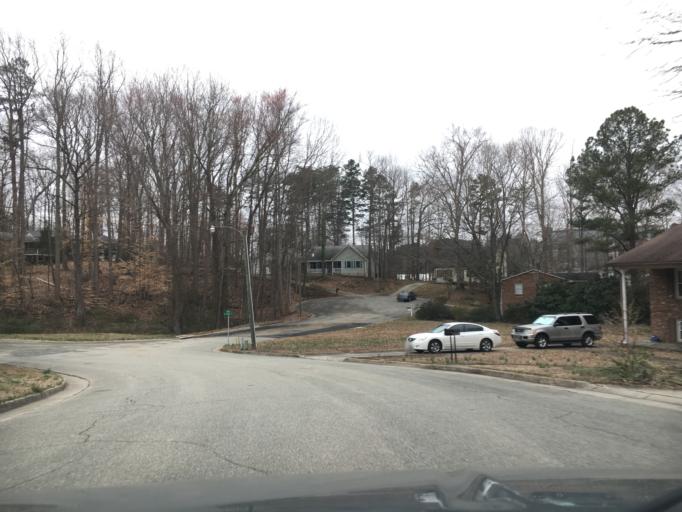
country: US
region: Virginia
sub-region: Halifax County
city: South Boston
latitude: 36.7143
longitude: -78.9094
